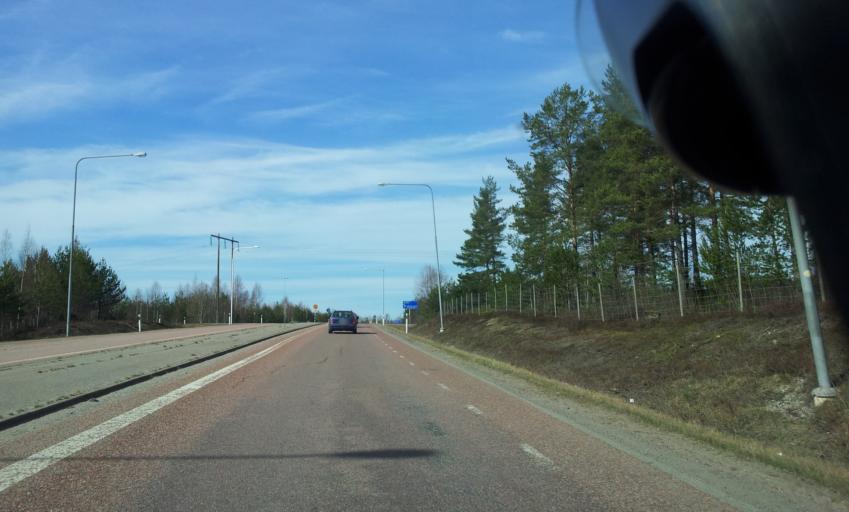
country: SE
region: Gaevleborg
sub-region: Hudiksvalls Kommun
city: Hudiksvall
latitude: 61.7138
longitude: 17.0774
